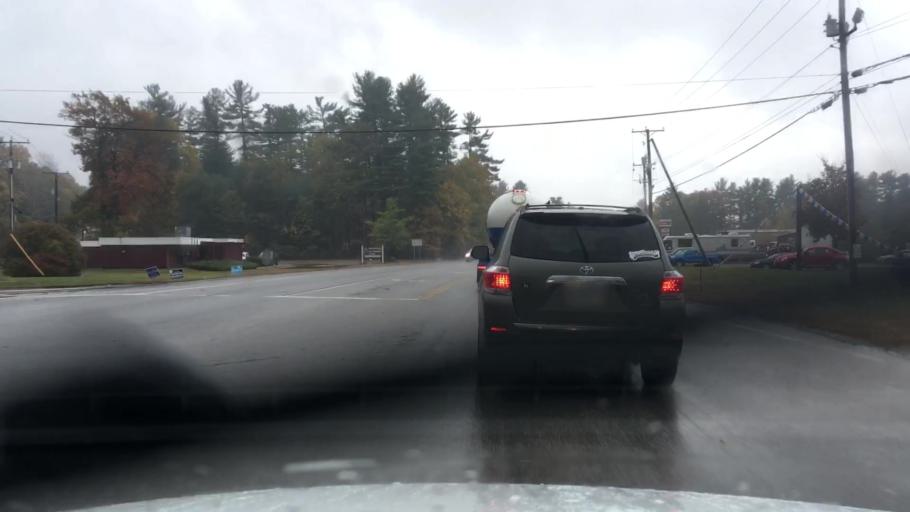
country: US
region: New Hampshire
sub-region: Strafford County
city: Rochester
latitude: 43.2540
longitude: -70.9793
